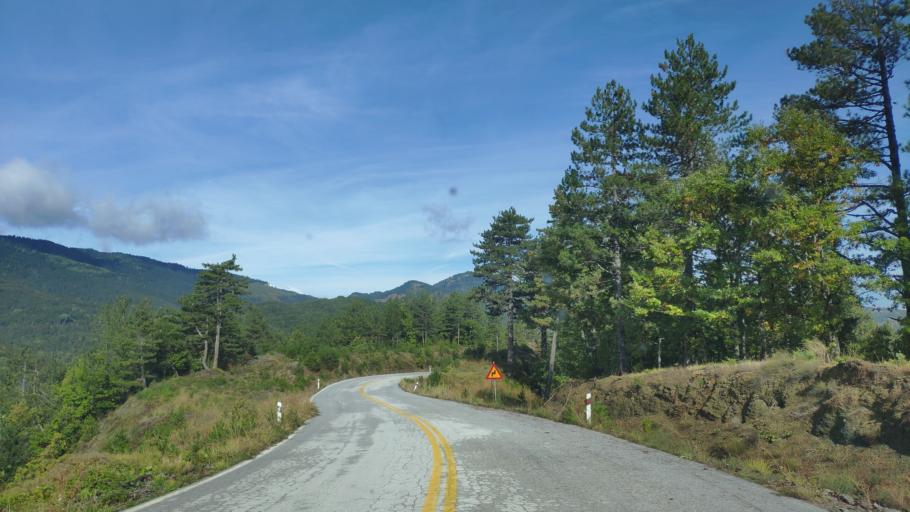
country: GR
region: West Macedonia
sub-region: Nomos Kastorias
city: Nestorio
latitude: 40.3656
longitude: 20.9467
